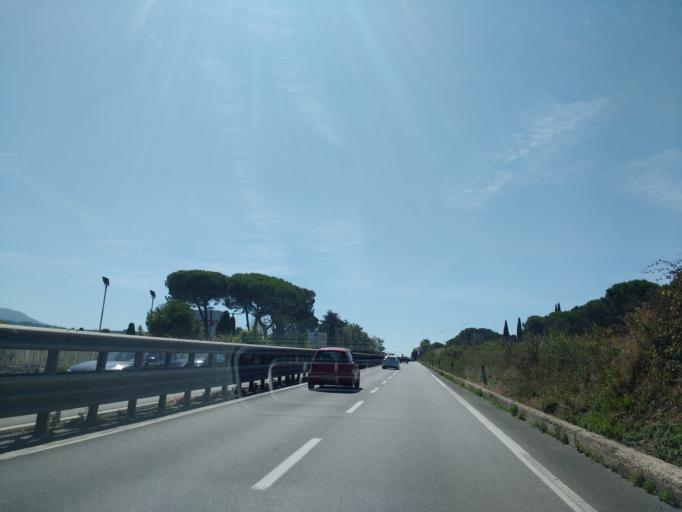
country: IT
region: Latium
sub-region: Citta metropolitana di Roma Capitale
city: Marino
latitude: 41.7709
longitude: 12.6124
